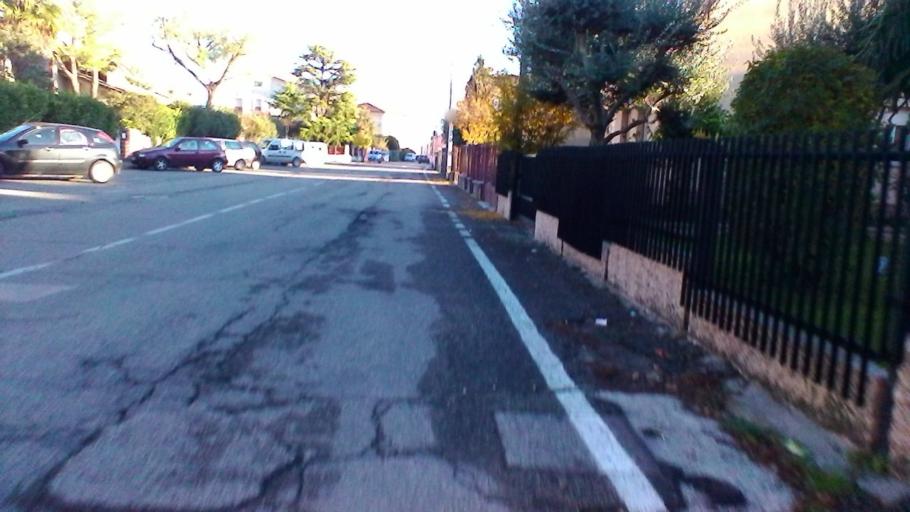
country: IT
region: Veneto
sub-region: Provincia di Verona
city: Povegliano Veronese
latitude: 45.3506
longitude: 10.8785
